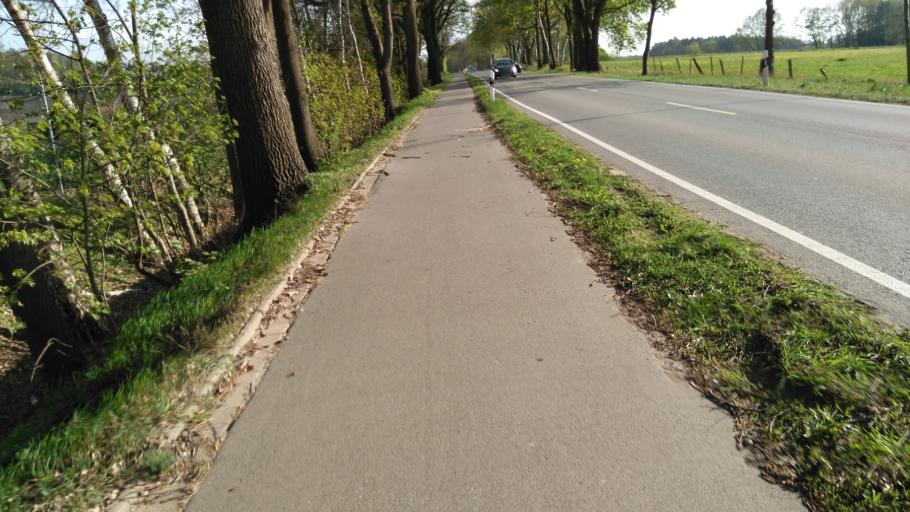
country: DE
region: Lower Saxony
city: Buxtehude
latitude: 53.4588
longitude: 9.6969
